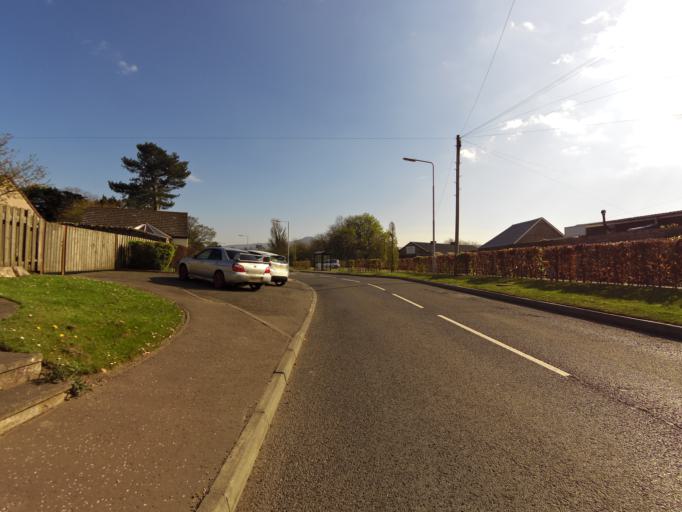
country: GB
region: Scotland
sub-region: Fife
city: Auchtermuchty
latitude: 56.2899
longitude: -3.2296
